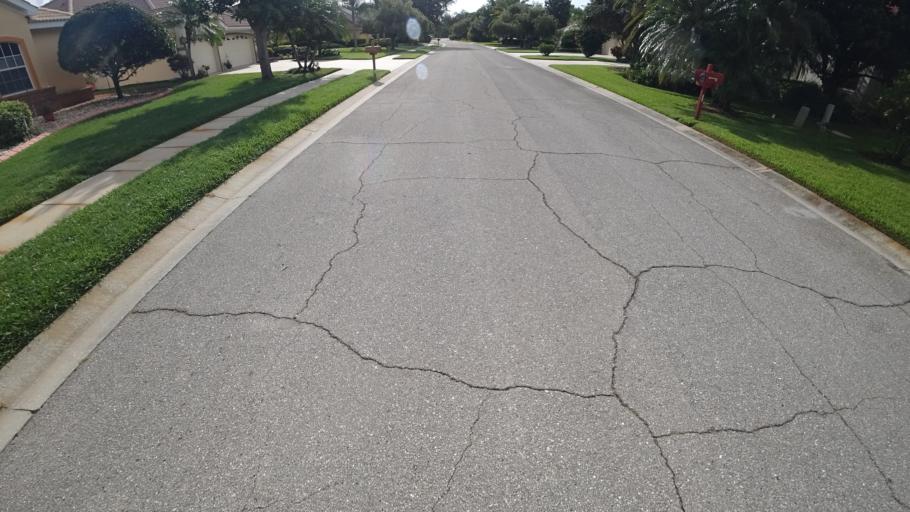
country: US
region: Florida
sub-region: Sarasota County
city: Desoto Lakes
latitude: 27.4148
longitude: -82.4795
